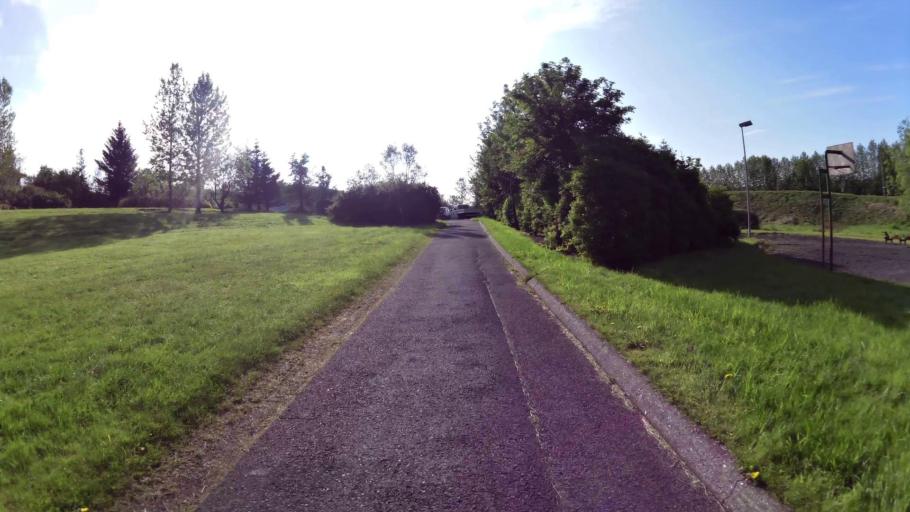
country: IS
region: Capital Region
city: Reykjavik
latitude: 64.1072
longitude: -21.8627
